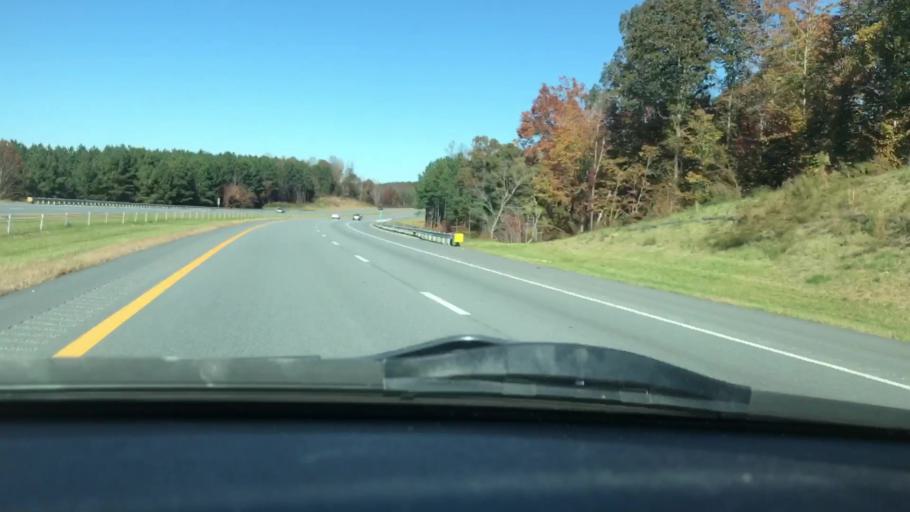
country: US
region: North Carolina
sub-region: Guilford County
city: Oak Ridge
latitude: 36.1603
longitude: -79.9584
